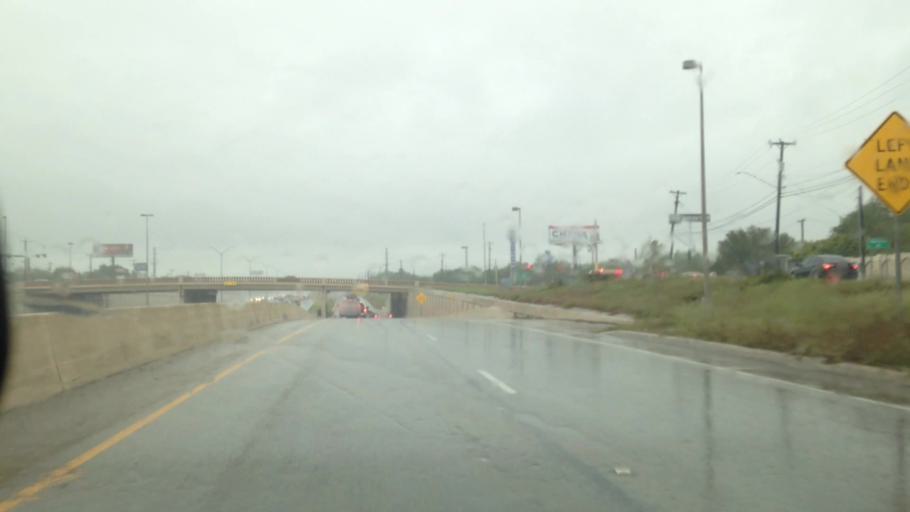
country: US
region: Texas
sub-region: Bexar County
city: Windcrest
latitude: 29.5158
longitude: -98.4248
